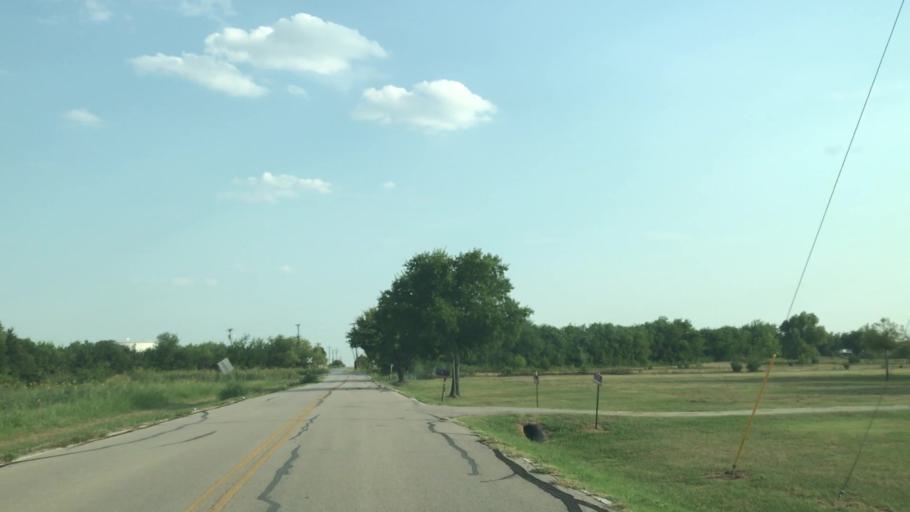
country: US
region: Texas
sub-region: Rockwall County
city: Fate
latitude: 32.9292
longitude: -96.4009
